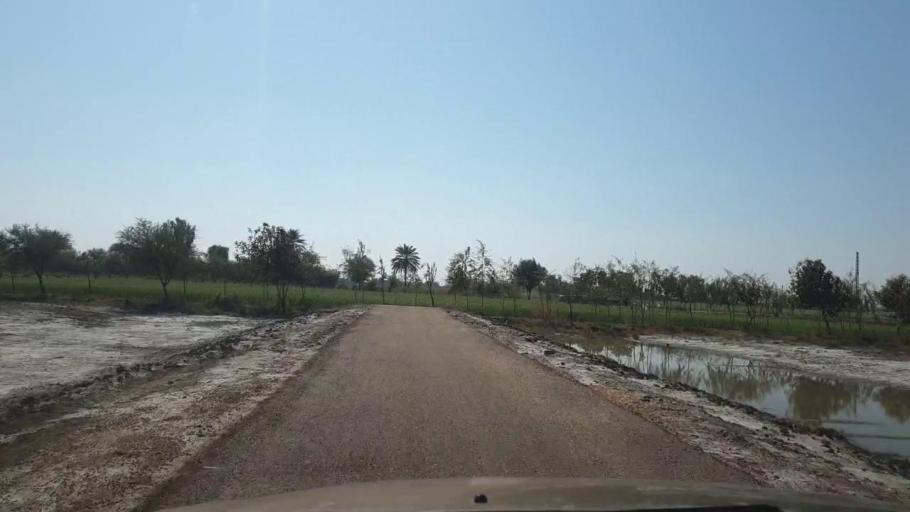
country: PK
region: Sindh
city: Mirpur Khas
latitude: 25.5685
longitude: 69.0585
